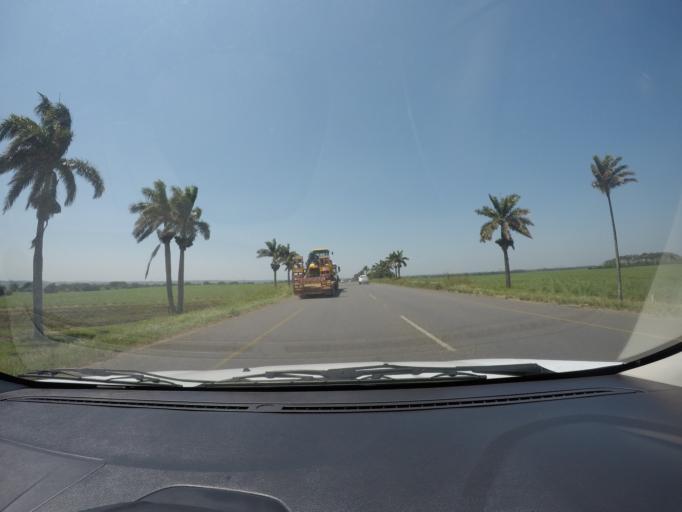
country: ZA
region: KwaZulu-Natal
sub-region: uThungulu District Municipality
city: Empangeni
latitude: -28.8098
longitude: 31.9562
